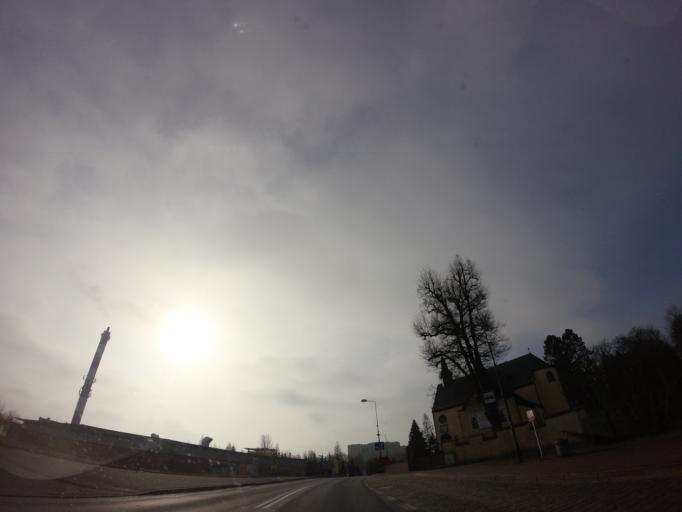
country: PL
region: West Pomeranian Voivodeship
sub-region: Powiat walecki
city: Walcz
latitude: 53.2672
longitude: 16.4622
